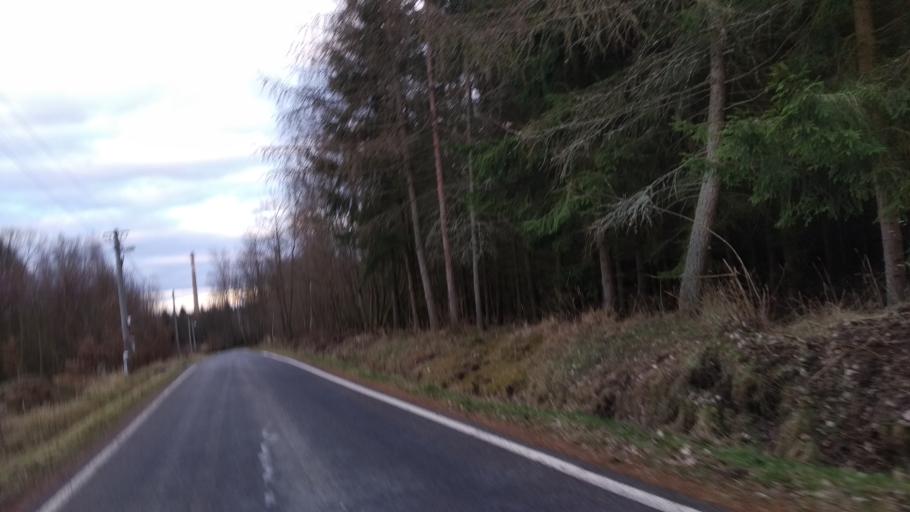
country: CZ
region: Karlovarsky
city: Kynsperk nad Ohri
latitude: 50.1251
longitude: 12.5477
